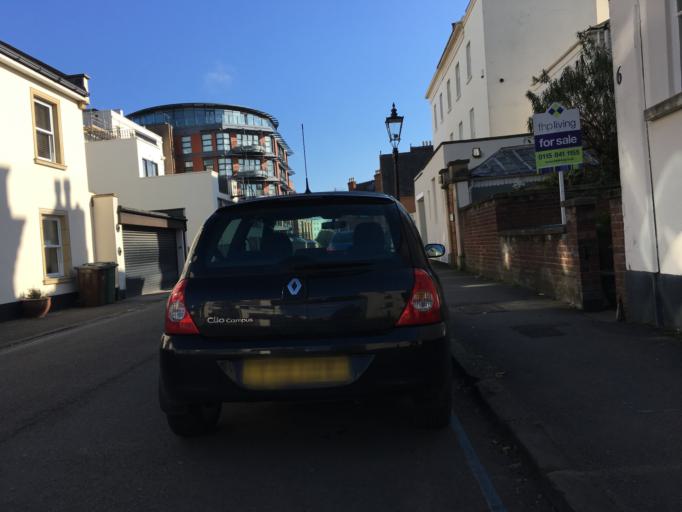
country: GB
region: England
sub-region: Nottingham
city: Nottingham
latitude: 52.9544
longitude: -1.1664
